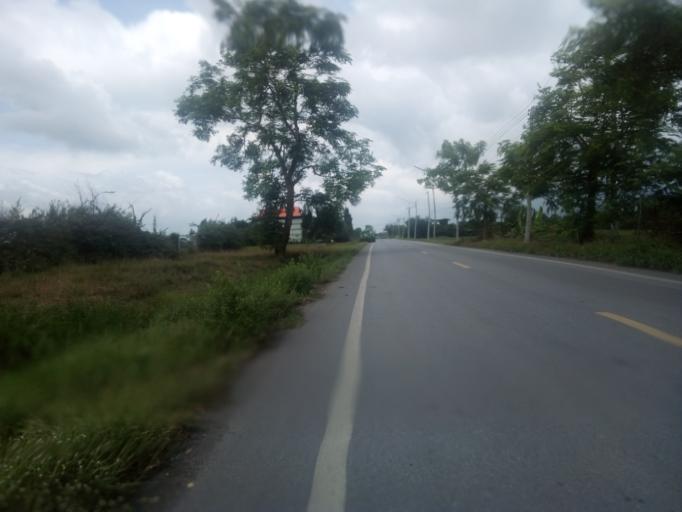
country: TH
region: Pathum Thani
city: Ban Lam Luk Ka
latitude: 13.9912
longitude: 100.8213
